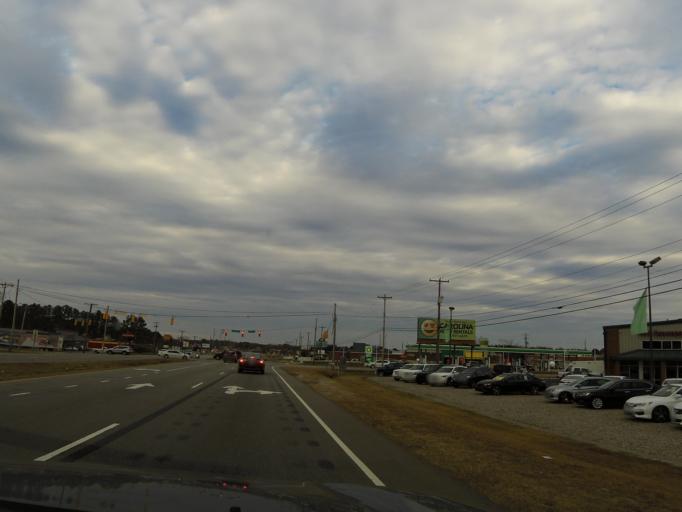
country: US
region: North Carolina
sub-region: Nash County
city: Rocky Mount
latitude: 35.9747
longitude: -77.7995
